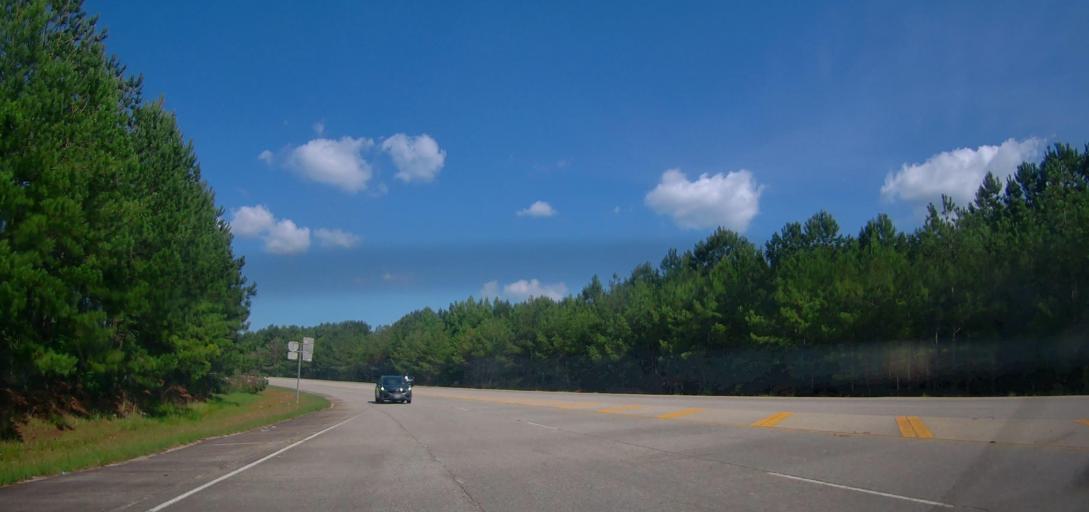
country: US
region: Georgia
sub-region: Henry County
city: Hampton
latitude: 33.3701
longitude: -84.3037
